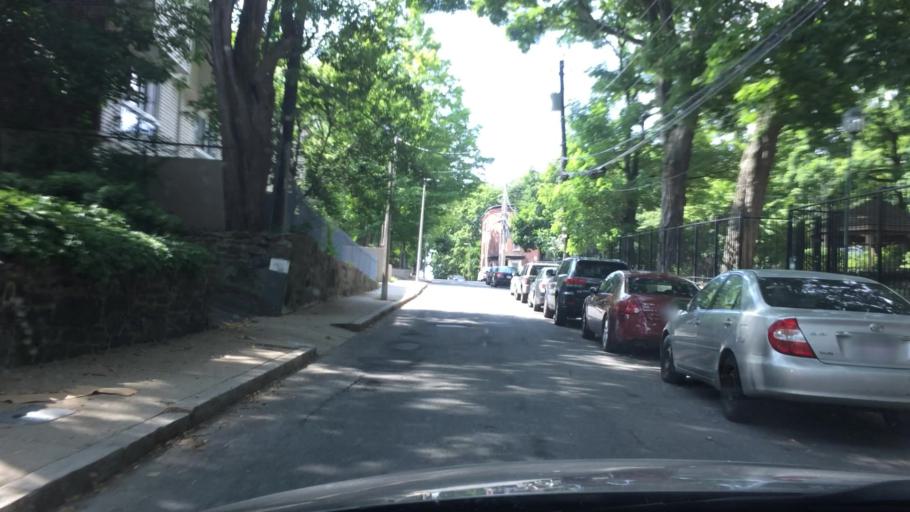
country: US
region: Massachusetts
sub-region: Norfolk County
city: Brookline
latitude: 42.3260
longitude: -71.0932
